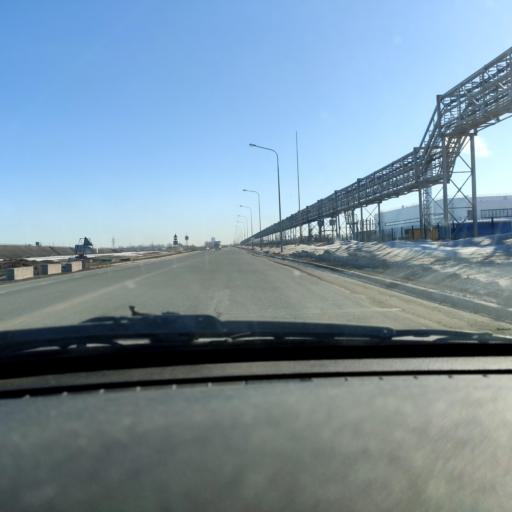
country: RU
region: Samara
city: Podstepki
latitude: 53.5605
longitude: 49.1898
